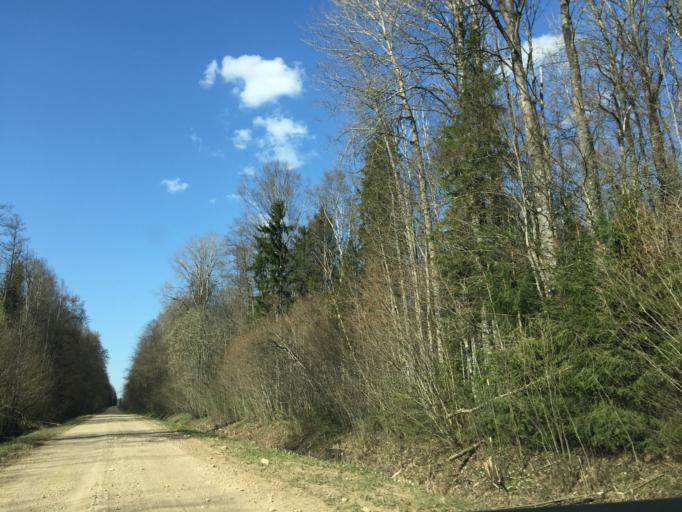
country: LV
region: Kegums
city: Kegums
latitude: 56.8618
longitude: 24.8016
